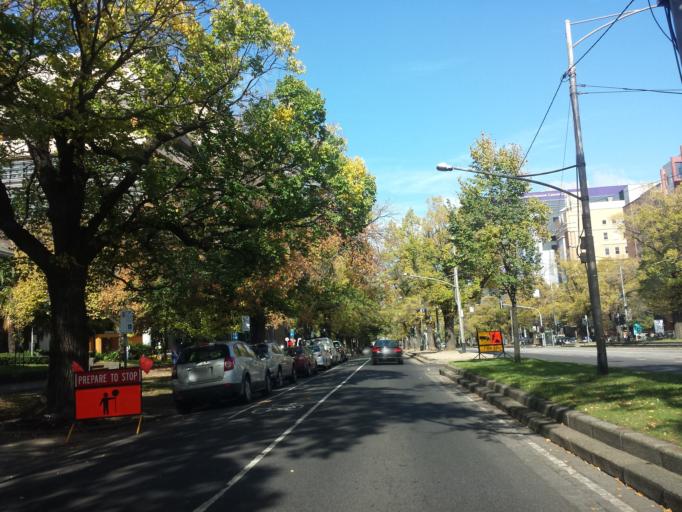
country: AU
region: Victoria
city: Carlton
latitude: -37.7974
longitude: 144.9580
